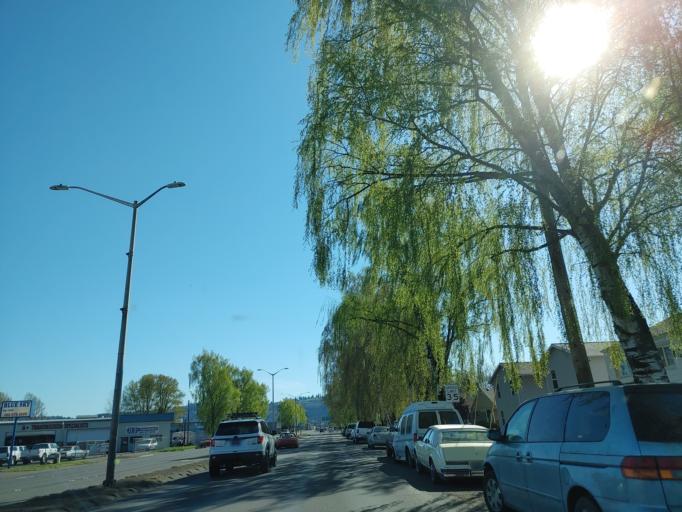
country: US
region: Washington
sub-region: Cowlitz County
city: Longview
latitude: 46.1210
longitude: -122.9467
